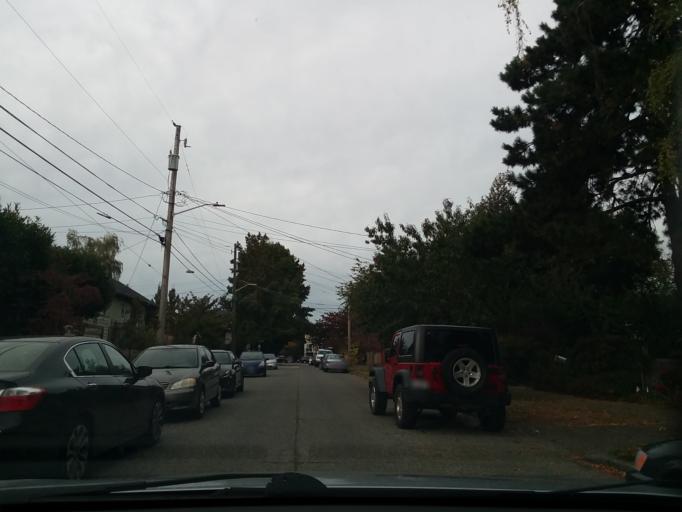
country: US
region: Washington
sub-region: King County
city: Shoreline
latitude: 47.6892
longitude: -122.3418
